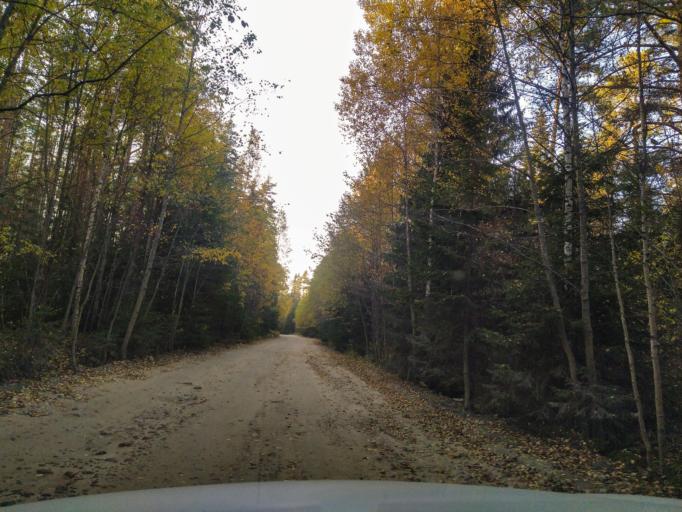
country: RU
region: Leningrad
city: Kuznechnoye
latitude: 61.3005
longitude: 30.0543
